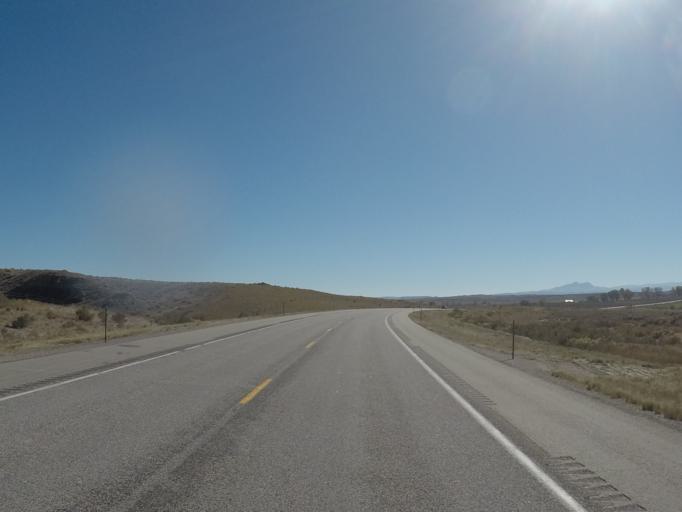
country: US
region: Montana
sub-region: Carbon County
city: Red Lodge
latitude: 44.9712
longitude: -109.0543
